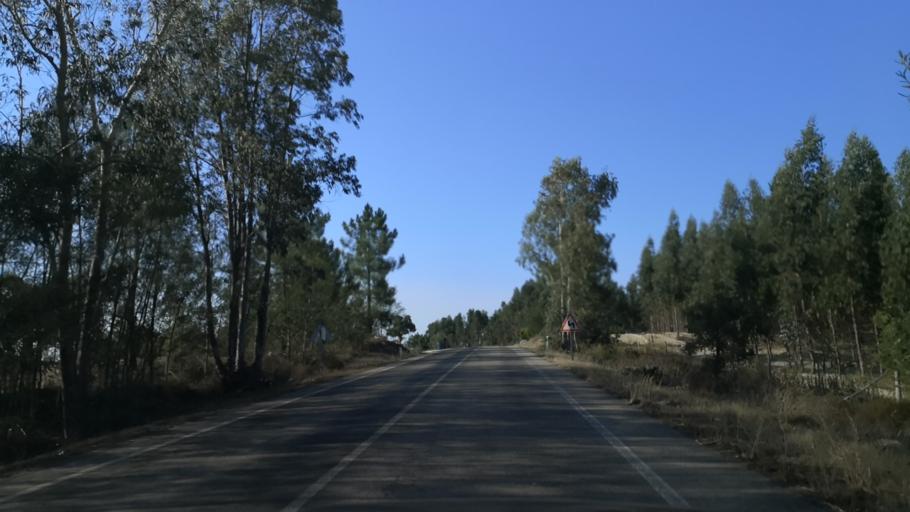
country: PT
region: Santarem
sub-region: Almeirim
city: Fazendas de Almeirim
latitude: 39.0967
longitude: -8.5756
